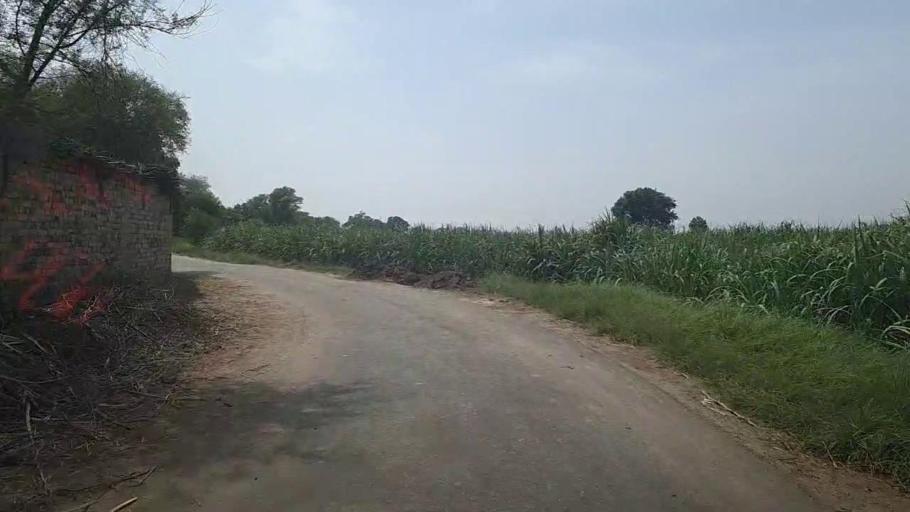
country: PK
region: Sindh
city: Ubauro
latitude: 28.1743
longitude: 69.8272
